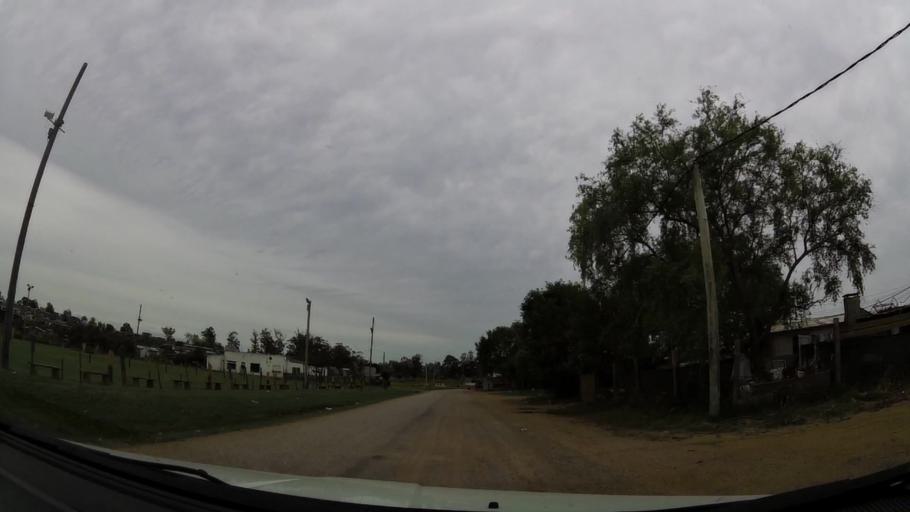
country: UY
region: Maldonado
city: Maldonado
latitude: -34.8900
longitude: -54.9580
